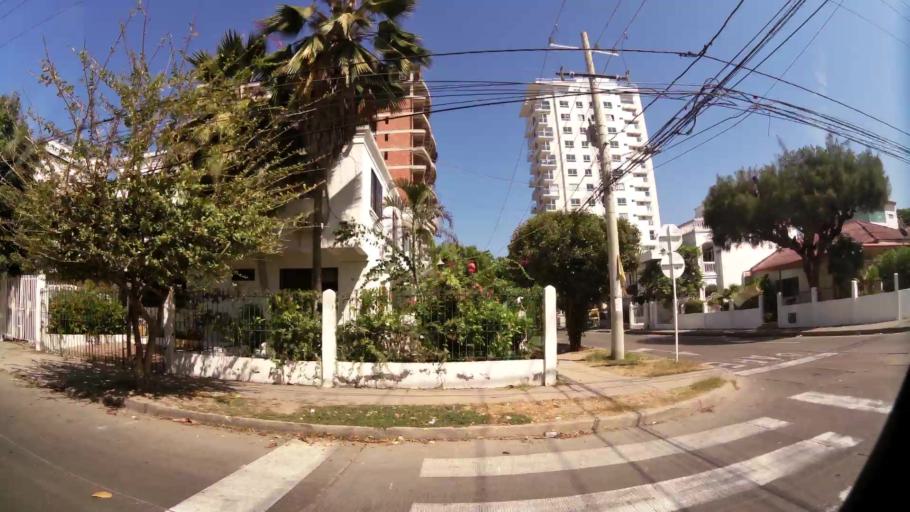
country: CO
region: Bolivar
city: Cartagena
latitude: 10.4437
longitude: -75.5198
